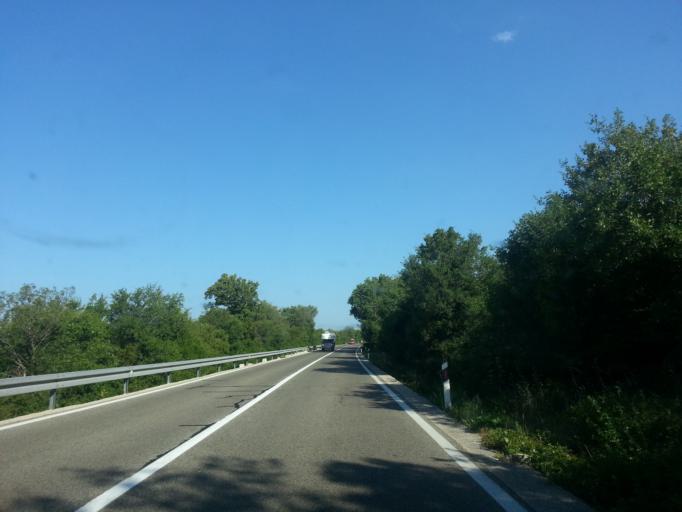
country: HR
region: Primorsko-Goranska
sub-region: Grad Crikvenica
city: Jadranovo
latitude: 45.2500
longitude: 14.6002
